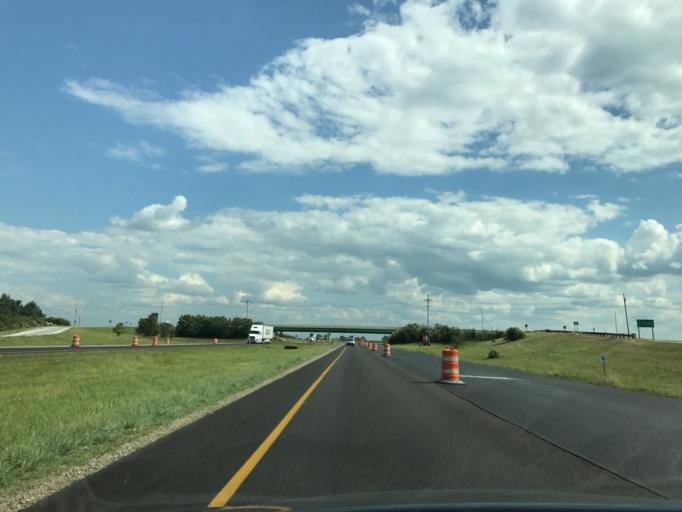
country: US
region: Ohio
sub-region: Van Wert County
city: Van Wert
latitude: 40.8813
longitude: -84.5270
